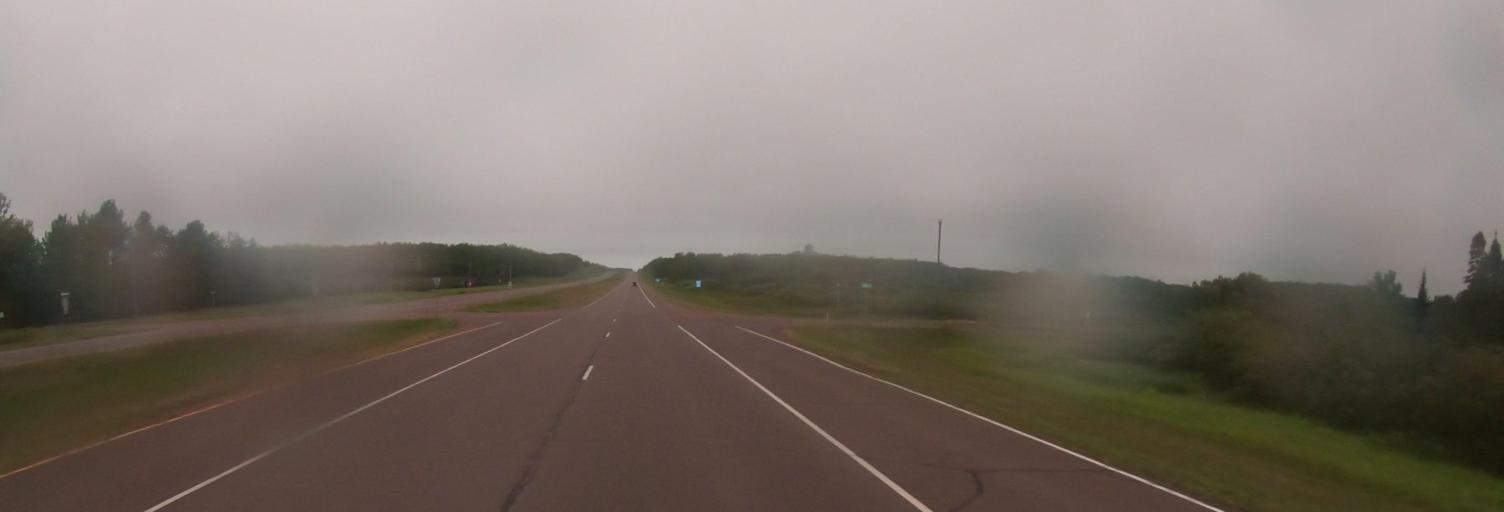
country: US
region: Minnesota
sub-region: Carlton County
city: Cloquet
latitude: 46.9228
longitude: -92.4693
